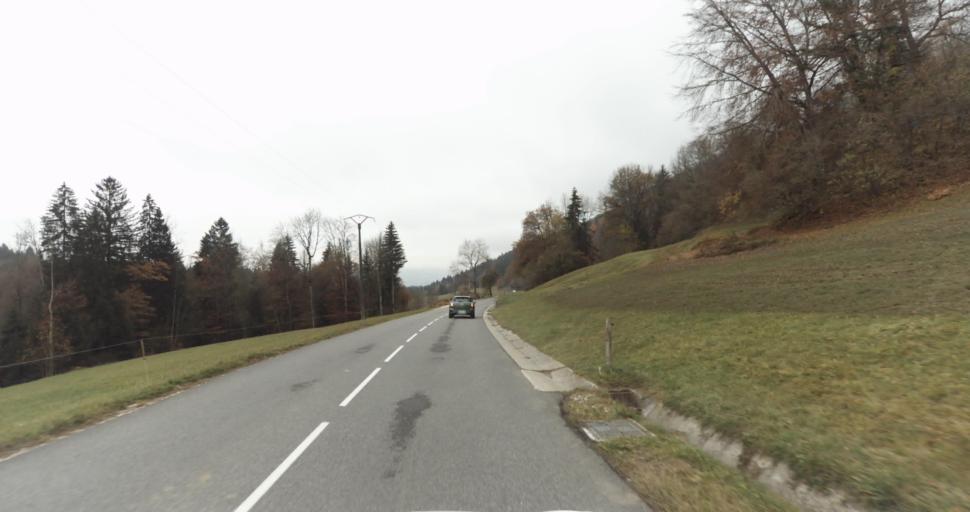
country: FR
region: Rhone-Alpes
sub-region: Departement de la Haute-Savoie
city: Gruffy
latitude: 45.7614
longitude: 6.1207
